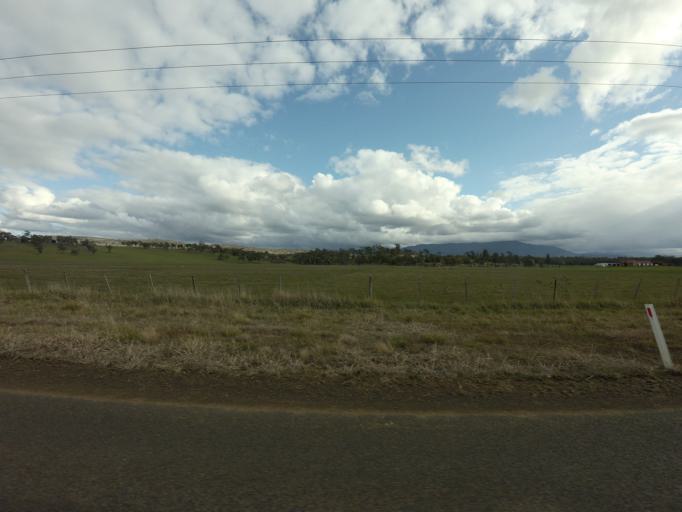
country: AU
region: Tasmania
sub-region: Northern Midlands
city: Evandale
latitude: -41.8689
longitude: 147.2916
